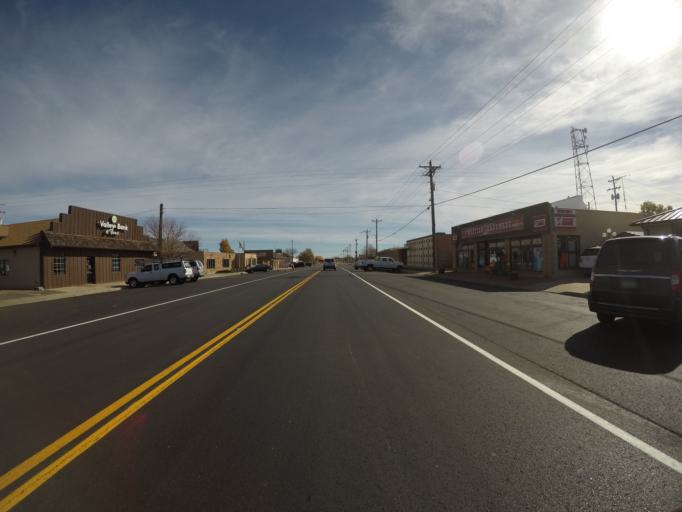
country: US
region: Colorado
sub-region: Adams County
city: Strasburg
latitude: 39.7383
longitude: -104.3247
